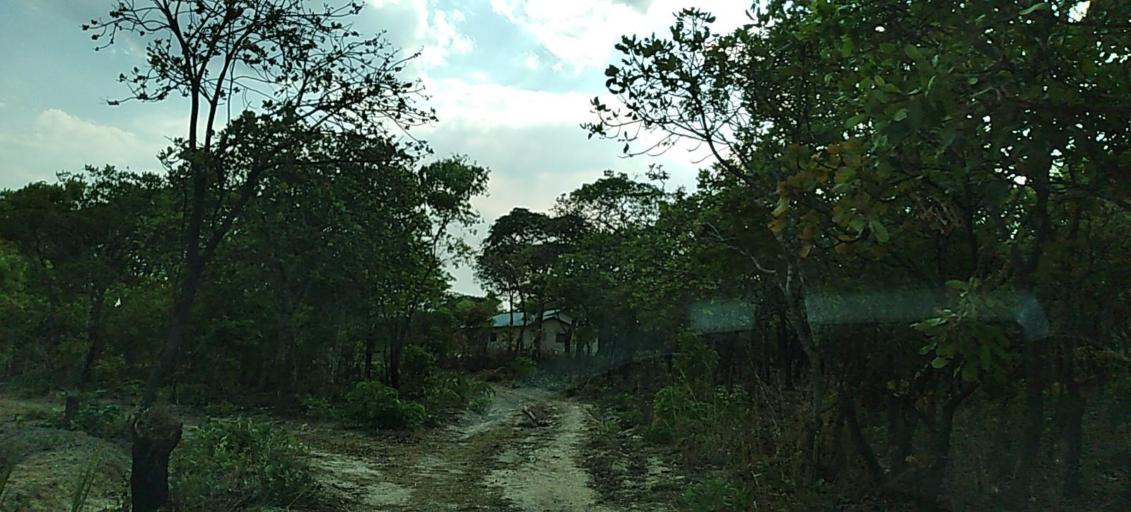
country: ZM
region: Copperbelt
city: Chililabombwe
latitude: -12.3546
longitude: 27.3978
